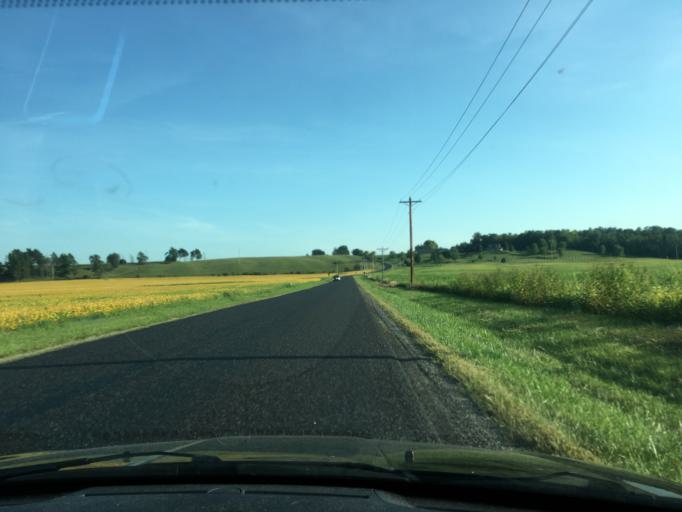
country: US
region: Ohio
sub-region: Logan County
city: West Liberty
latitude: 40.2771
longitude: -83.7244
